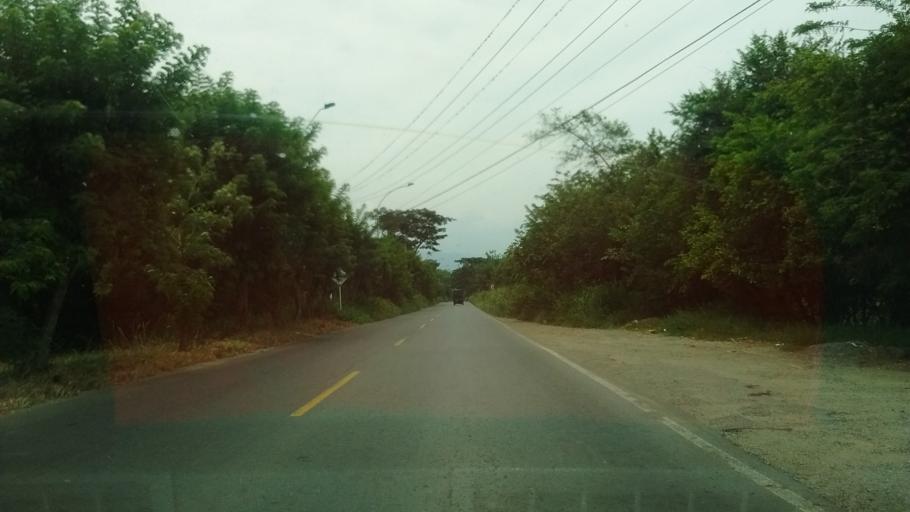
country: CO
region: Valle del Cauca
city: Jamundi
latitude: 3.3374
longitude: -76.5166
